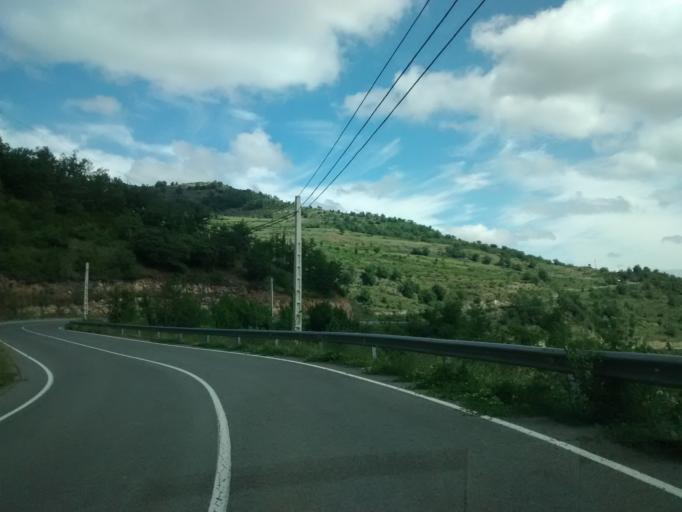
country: ES
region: La Rioja
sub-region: Provincia de La Rioja
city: Soto en Cameros
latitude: 42.3022
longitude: -2.4191
